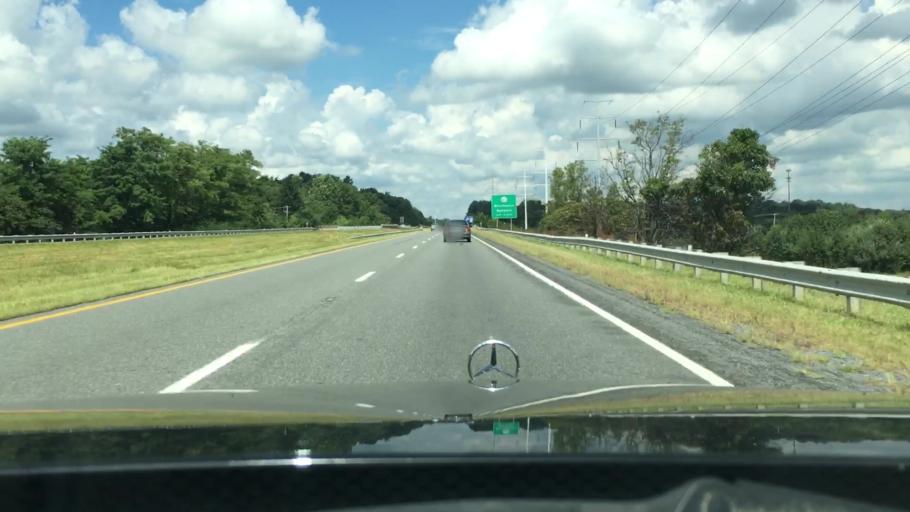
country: US
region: Virginia
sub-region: Frederick County
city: Stephens City
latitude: 39.1410
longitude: -78.2096
